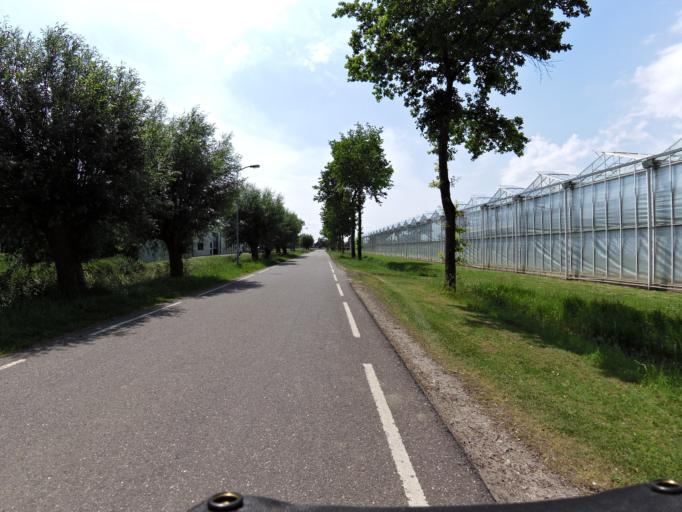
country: NL
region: North Brabant
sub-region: Gemeente Aalburg
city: Aalburg
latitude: 51.7959
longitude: 5.1021
